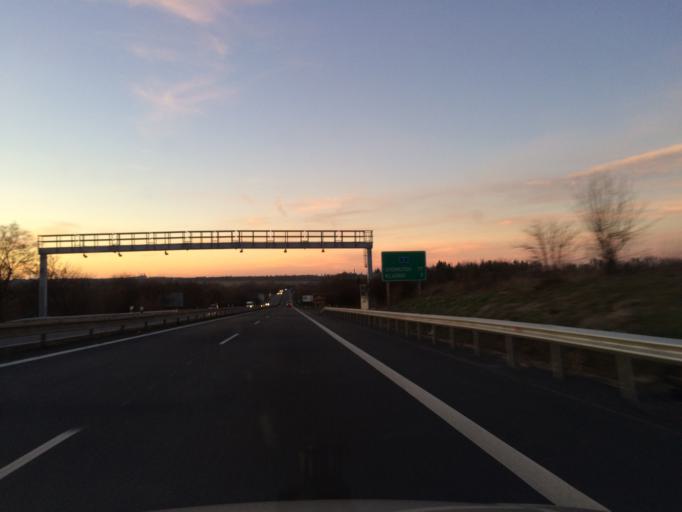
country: CZ
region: Central Bohemia
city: Tuchomerice
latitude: 50.1382
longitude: 14.2423
